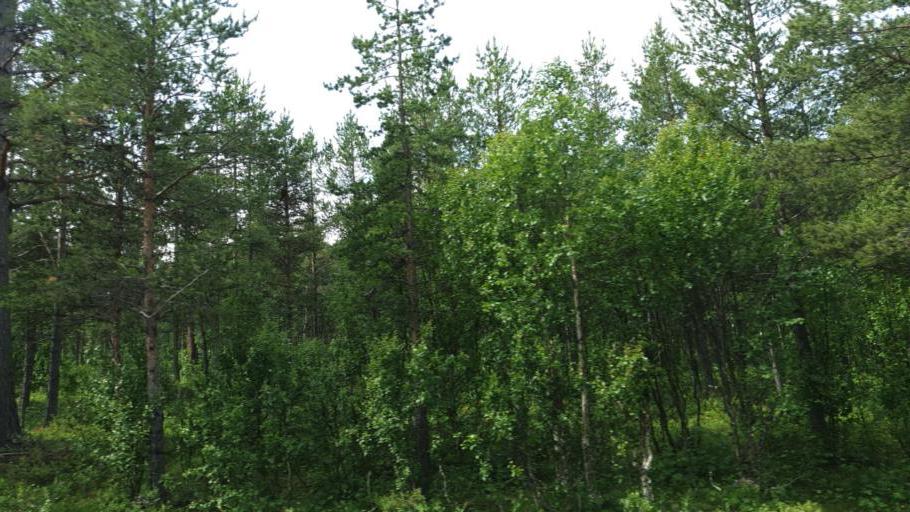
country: NO
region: Oppland
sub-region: Vaga
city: Vagamo
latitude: 61.6998
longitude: 9.0593
